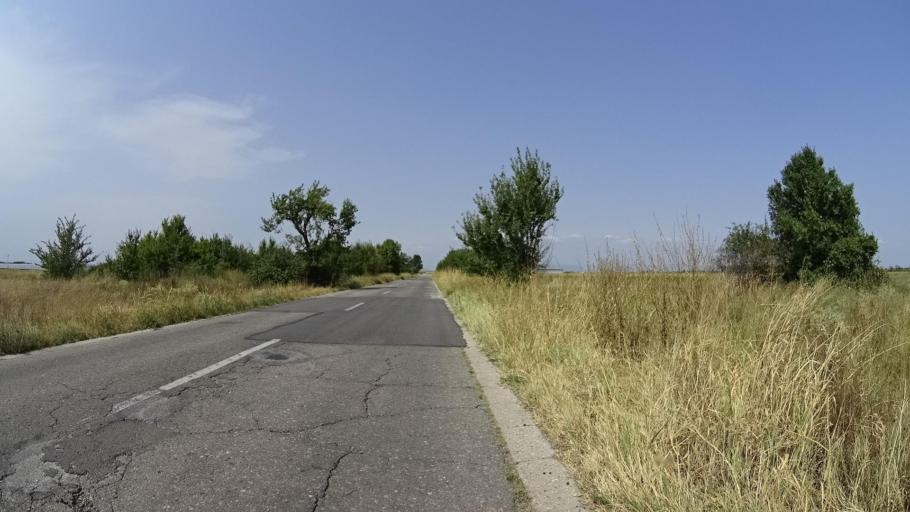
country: BG
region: Plovdiv
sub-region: Obshtina Plovdiv
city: Plovdiv
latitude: 42.2249
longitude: 24.7857
